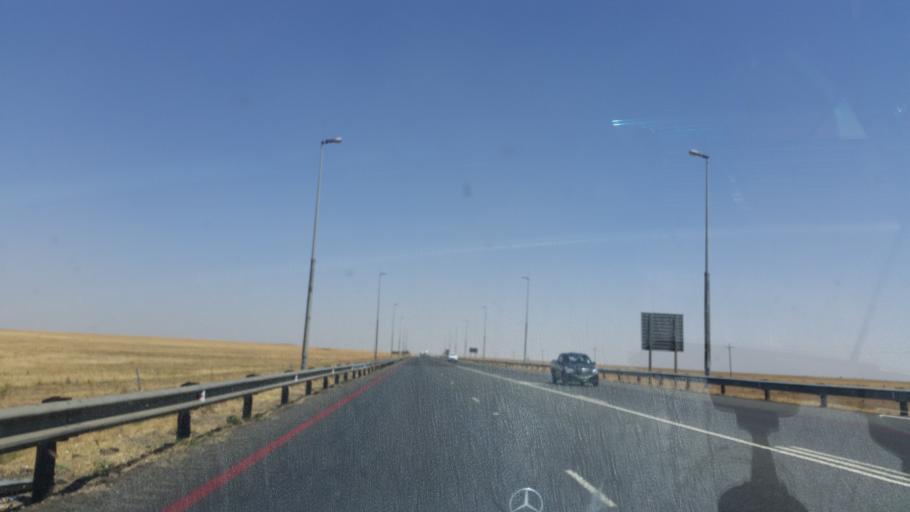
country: ZA
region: Orange Free State
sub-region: Lejweleputswa District Municipality
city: Brandfort
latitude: -28.8001
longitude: 26.6887
